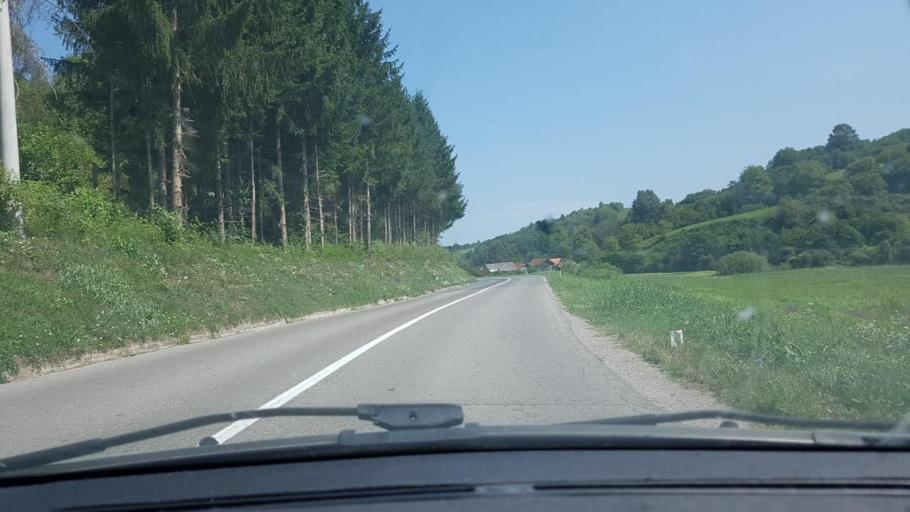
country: HR
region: Karlovacka
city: Vojnic
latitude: 45.2891
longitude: 15.6700
